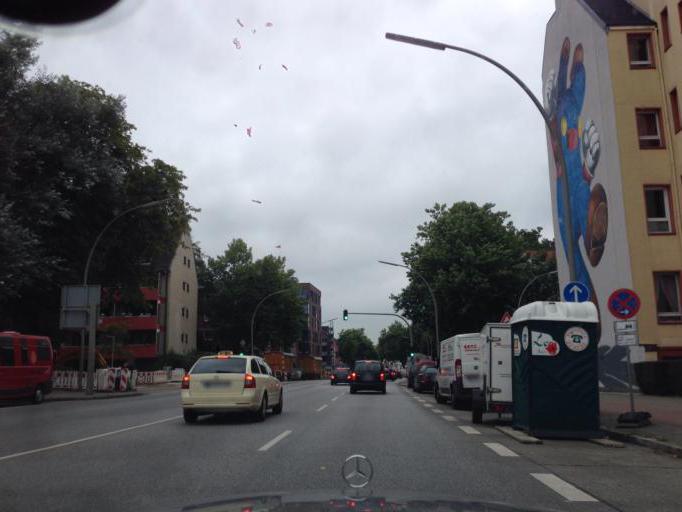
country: DE
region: Hamburg
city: St. Pauli
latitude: 53.5720
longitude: 9.9576
